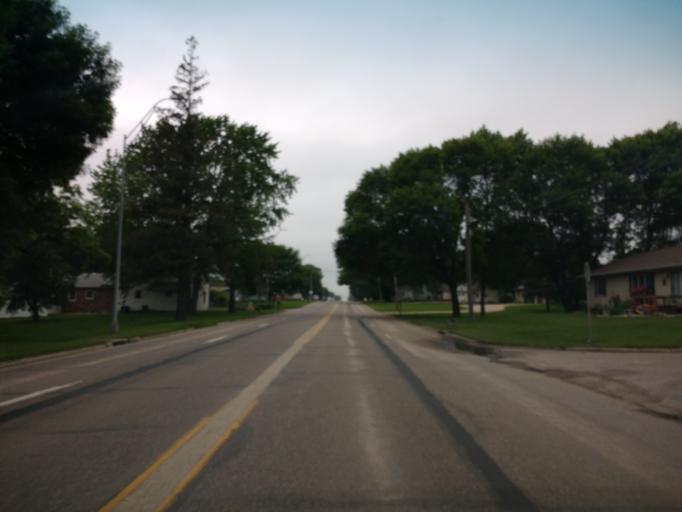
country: US
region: Iowa
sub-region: O'Brien County
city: Hartley
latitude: 43.1848
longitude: -95.4676
